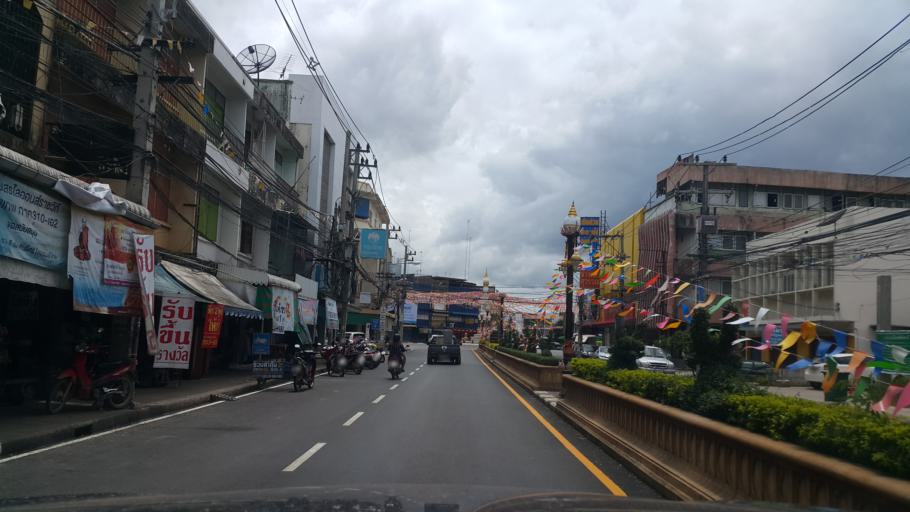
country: TH
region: Sukhothai
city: Sukhothai
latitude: 17.0095
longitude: 99.8208
